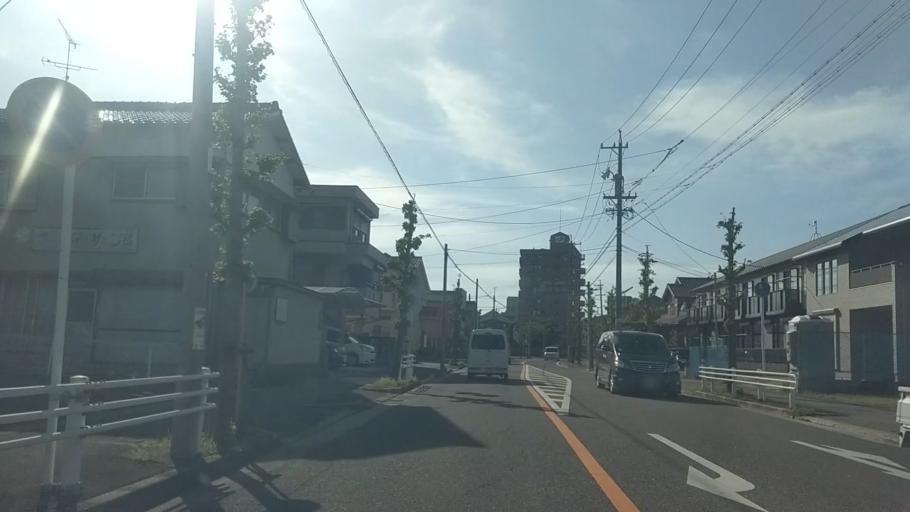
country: JP
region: Aichi
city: Anjo
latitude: 34.9560
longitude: 137.0928
